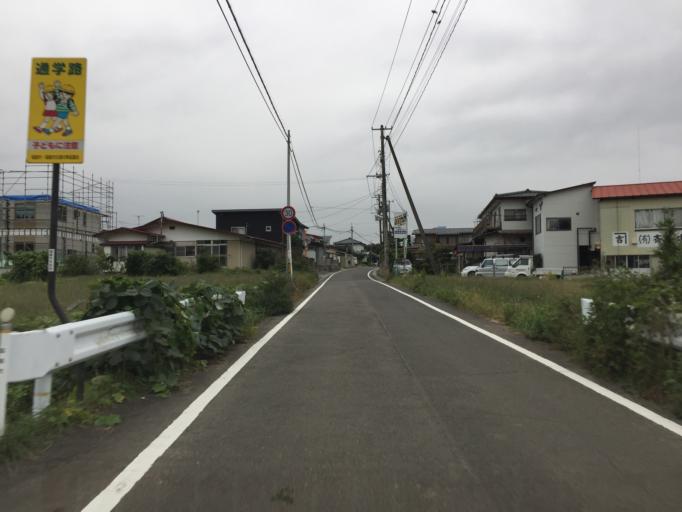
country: JP
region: Fukushima
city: Nihommatsu
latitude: 37.6552
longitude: 140.4687
